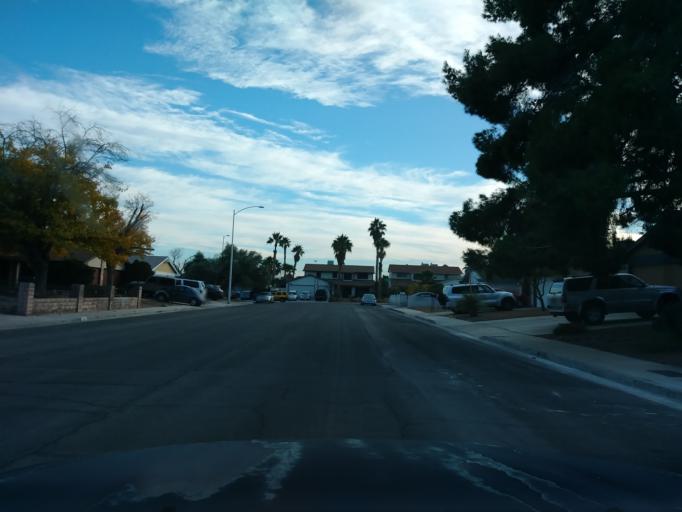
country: US
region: Nevada
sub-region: Clark County
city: Spring Valley
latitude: 36.1680
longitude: -115.2386
